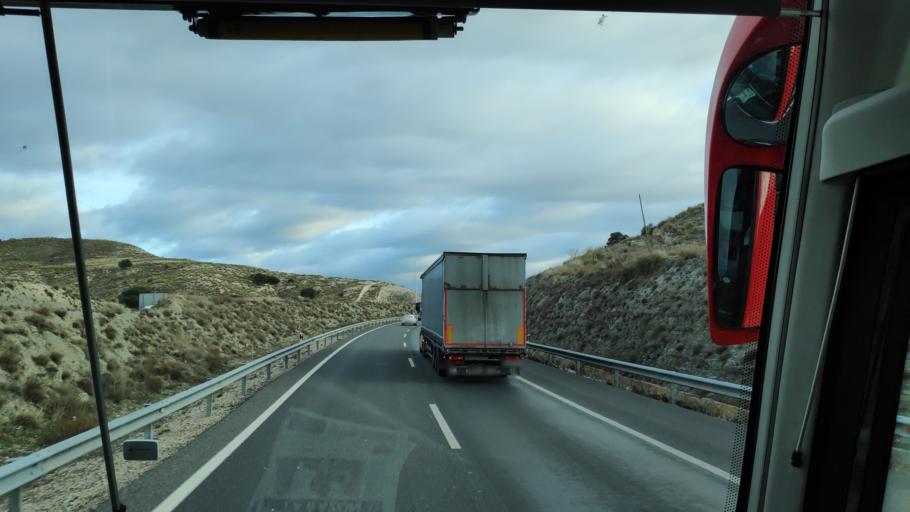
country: ES
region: Madrid
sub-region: Provincia de Madrid
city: Perales de Tajuna
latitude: 40.2138
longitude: -3.3271
